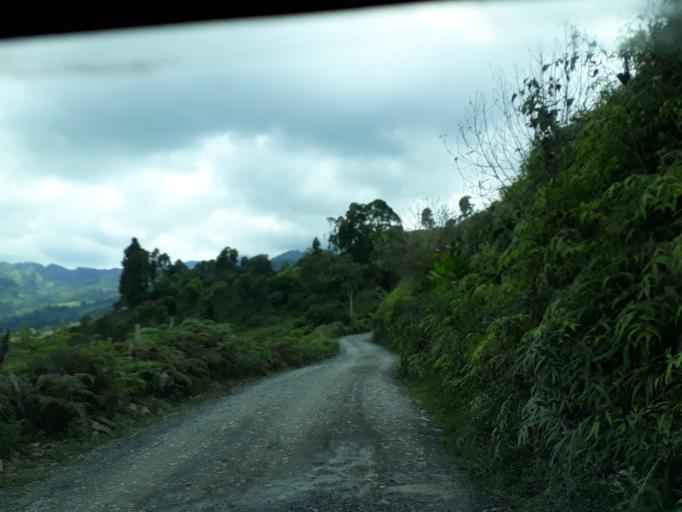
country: CO
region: Cundinamarca
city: Topaipi
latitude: 5.2910
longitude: -74.1955
